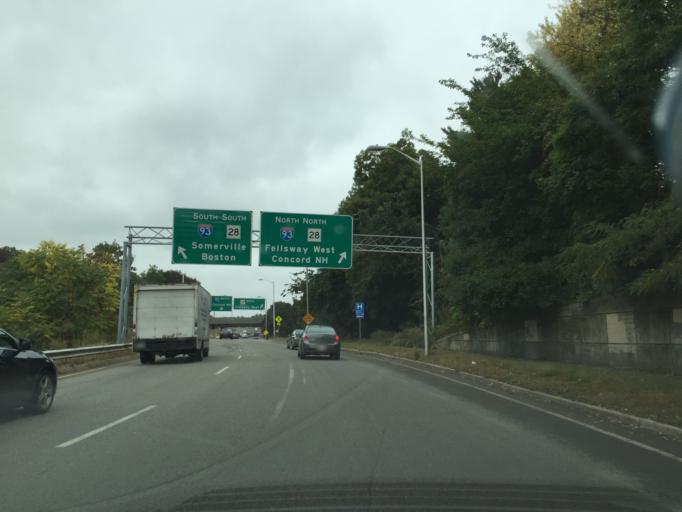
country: US
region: Massachusetts
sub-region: Middlesex County
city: Medford
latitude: 42.4289
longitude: -71.1025
